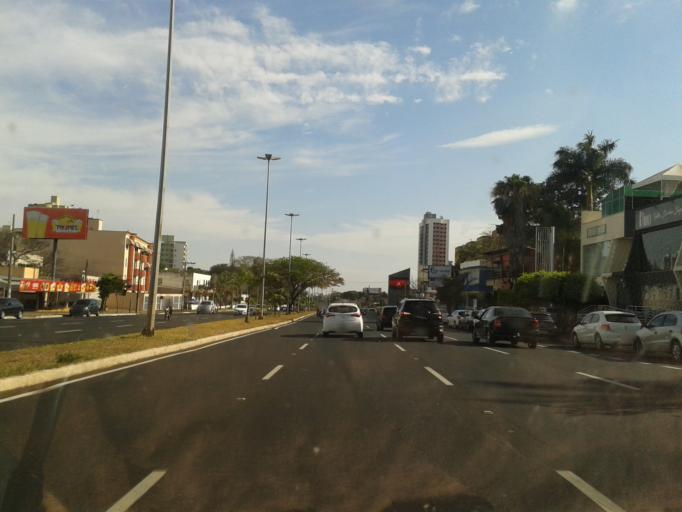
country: BR
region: Minas Gerais
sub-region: Uberlandia
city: Uberlandia
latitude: -18.9196
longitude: -48.2675
